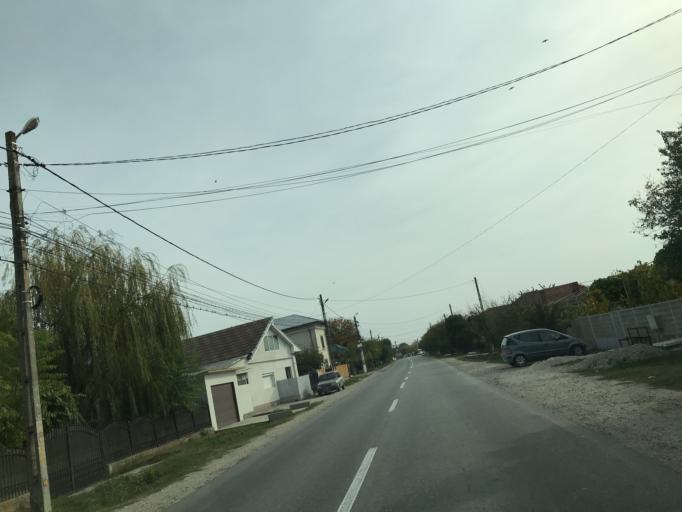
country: RO
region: Olt
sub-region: Comuna Slatioara
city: Slatioara
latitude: 44.4019
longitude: 24.3255
